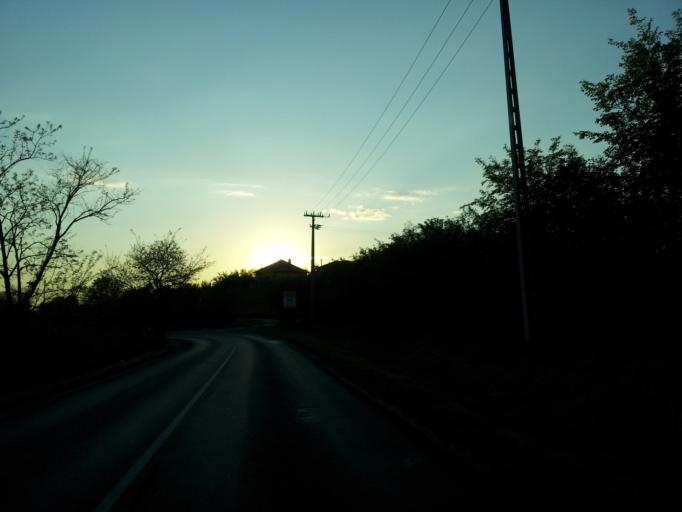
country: HU
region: Pest
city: Perbal
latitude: 47.6205
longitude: 18.7874
